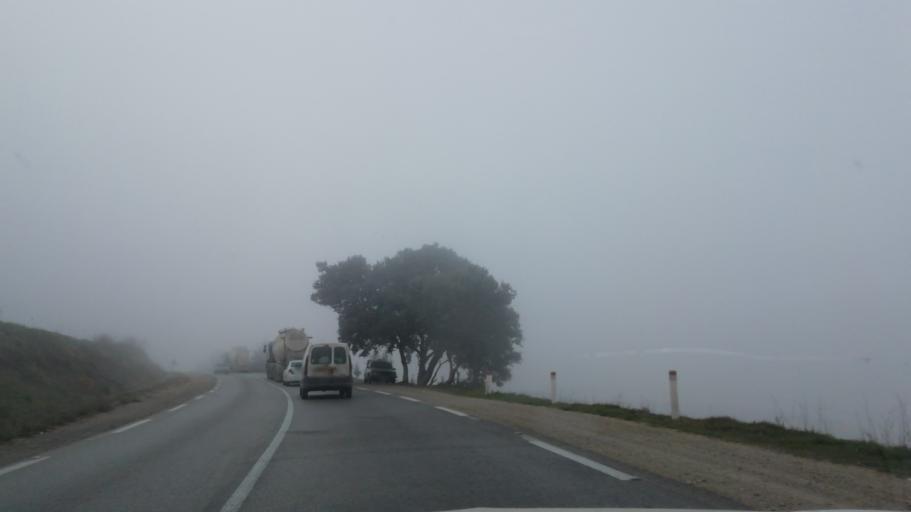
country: DZ
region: Mascara
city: Mascara
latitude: 35.5273
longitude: 0.3263
